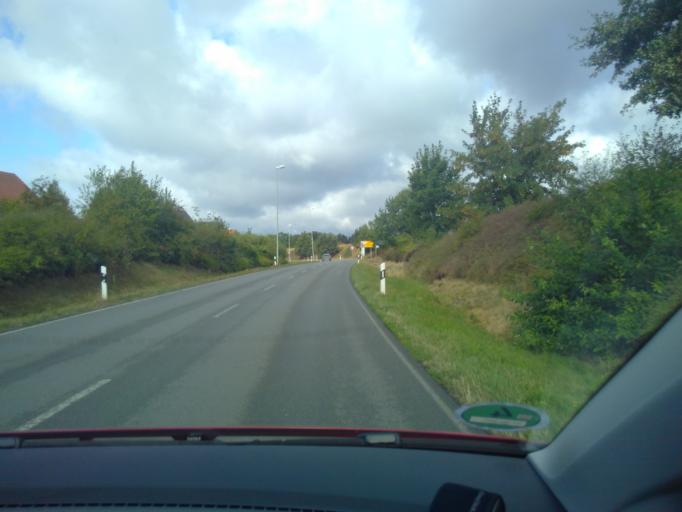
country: DE
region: North Rhine-Westphalia
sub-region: Regierungsbezirk Munster
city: Warendorf
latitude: 51.9636
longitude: 7.9836
